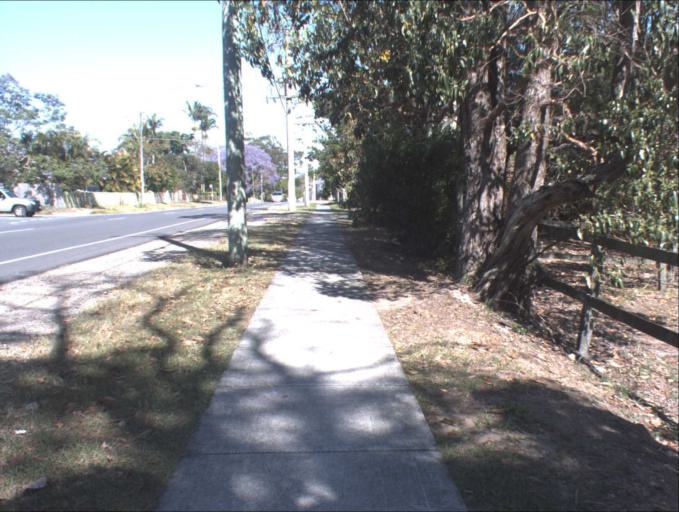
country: AU
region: Queensland
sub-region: Logan
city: Rochedale South
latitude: -27.5950
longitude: 153.1194
